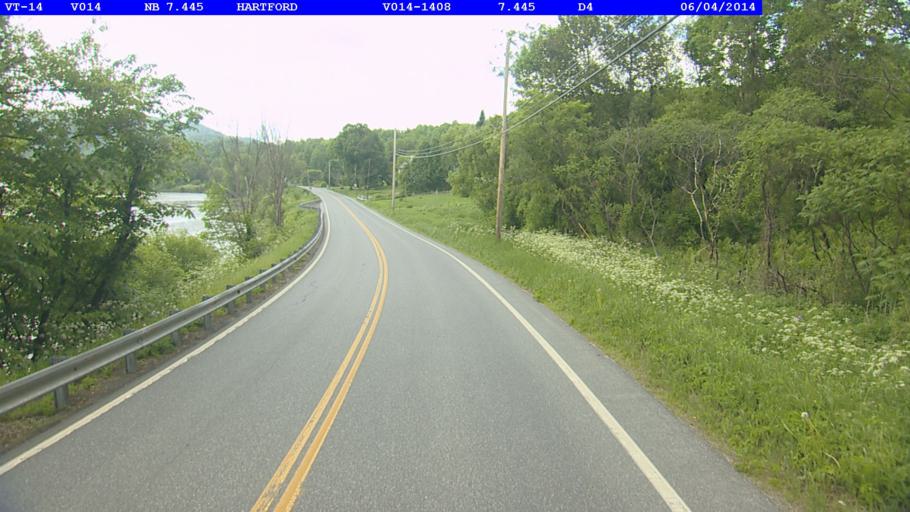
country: US
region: Vermont
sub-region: Windsor County
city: Wilder
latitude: 43.7200
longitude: -72.4190
